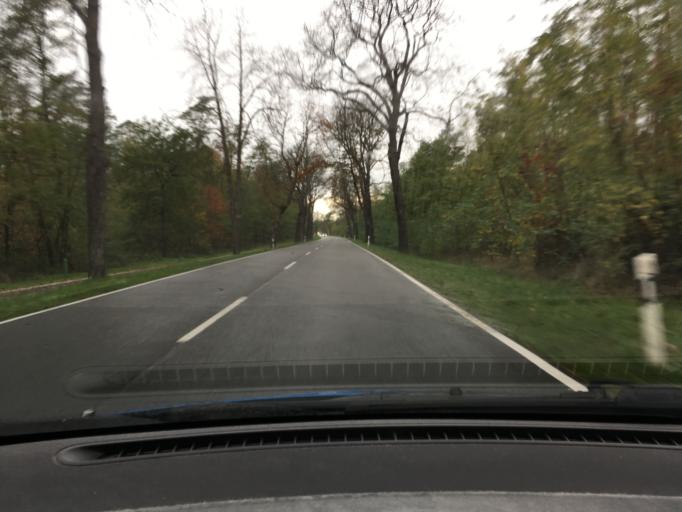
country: DE
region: Saxony-Anhalt
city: Rodleben
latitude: 51.9201
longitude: 12.1710
